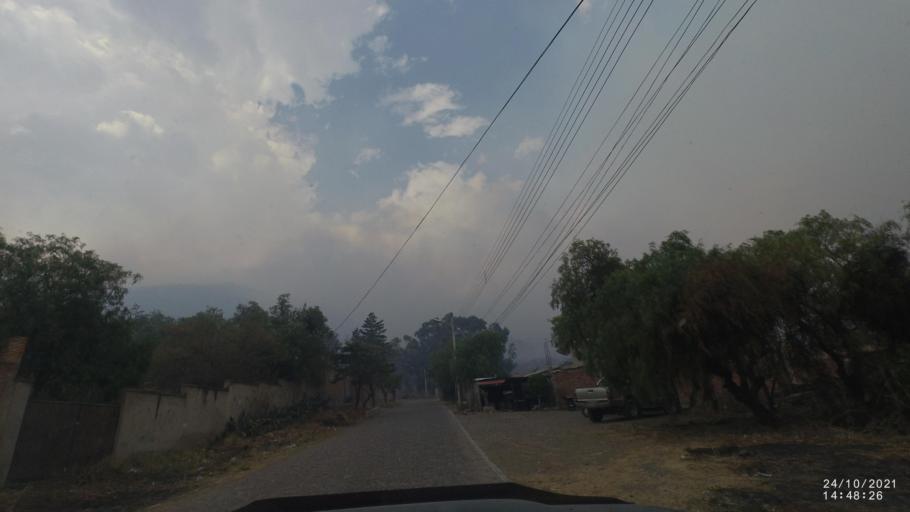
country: BO
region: Cochabamba
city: Cochabamba
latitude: -17.3513
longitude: -66.1510
